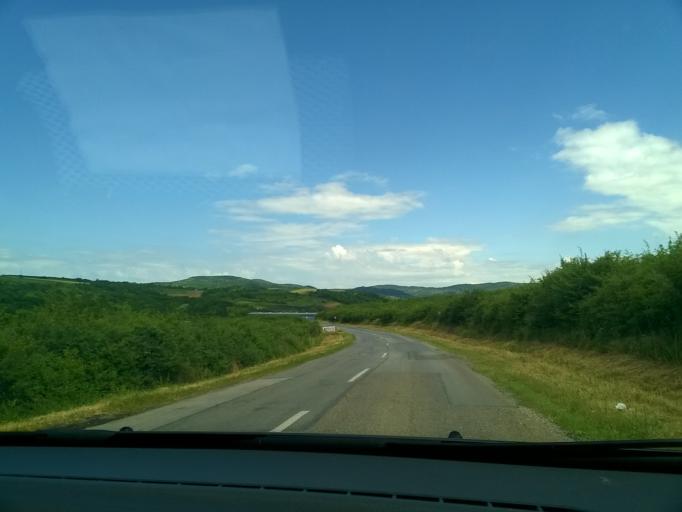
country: RS
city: Vrdnik
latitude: 45.1017
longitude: 19.8034
